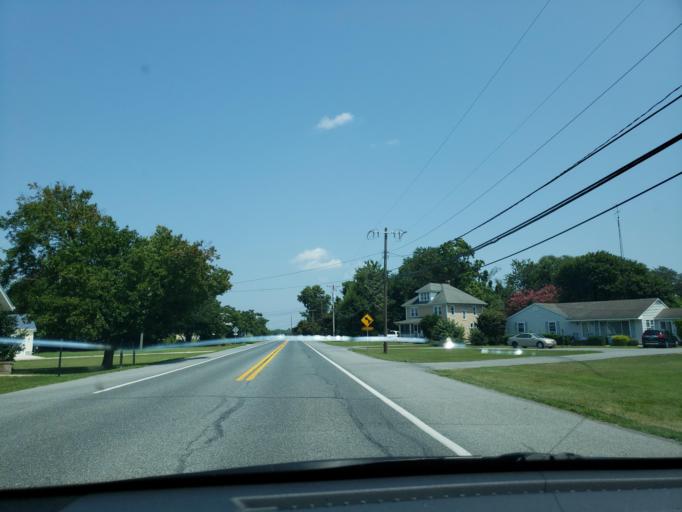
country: US
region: Delaware
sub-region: Sussex County
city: Milton
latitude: 38.7909
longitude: -75.3155
